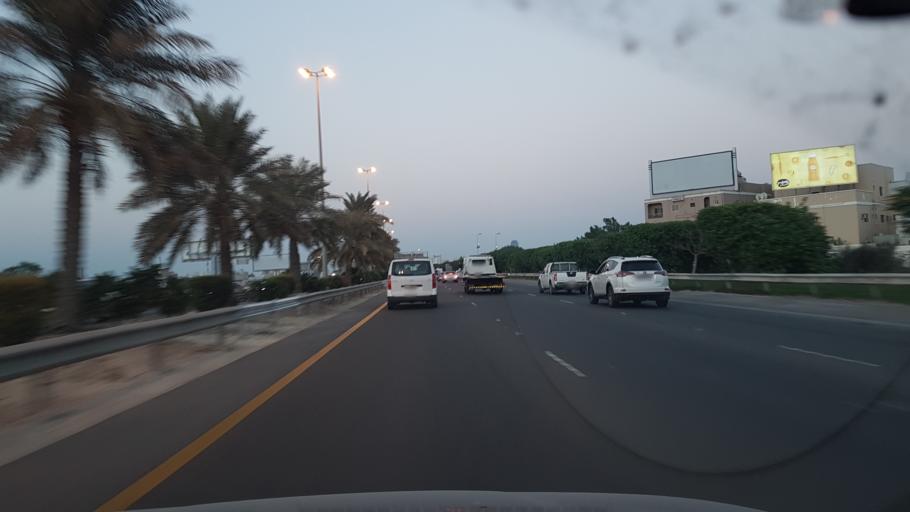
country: BH
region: Manama
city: Jidd Hafs
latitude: 26.2071
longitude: 50.5162
